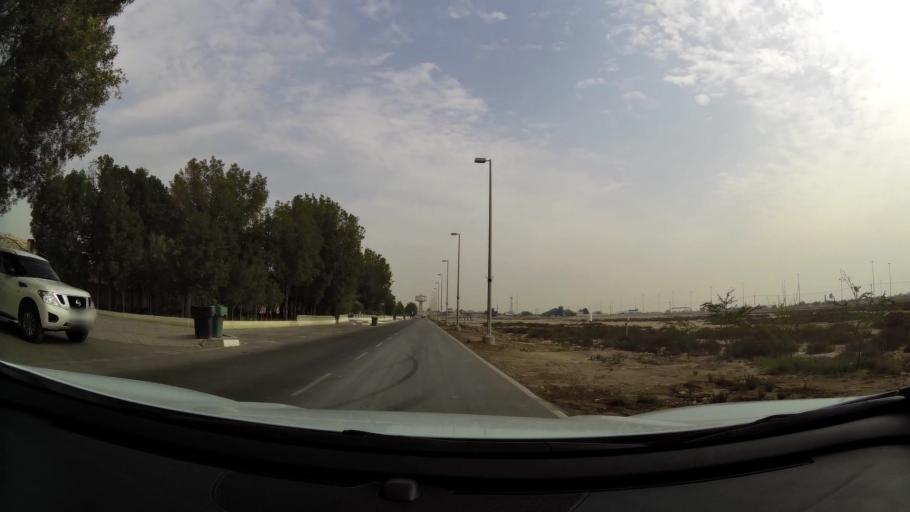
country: AE
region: Abu Dhabi
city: Abu Dhabi
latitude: 24.6754
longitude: 54.7606
